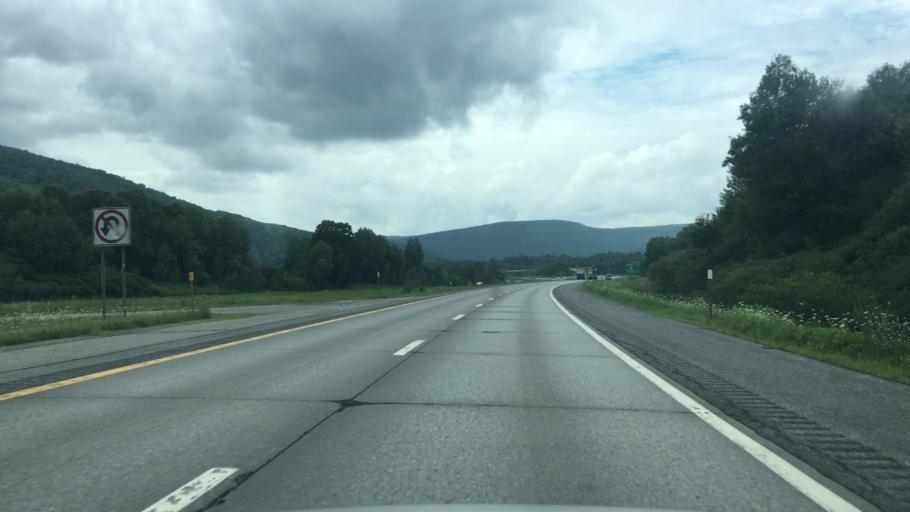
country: US
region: New York
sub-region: Otsego County
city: Worcester
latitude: 42.5952
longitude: -74.7161
